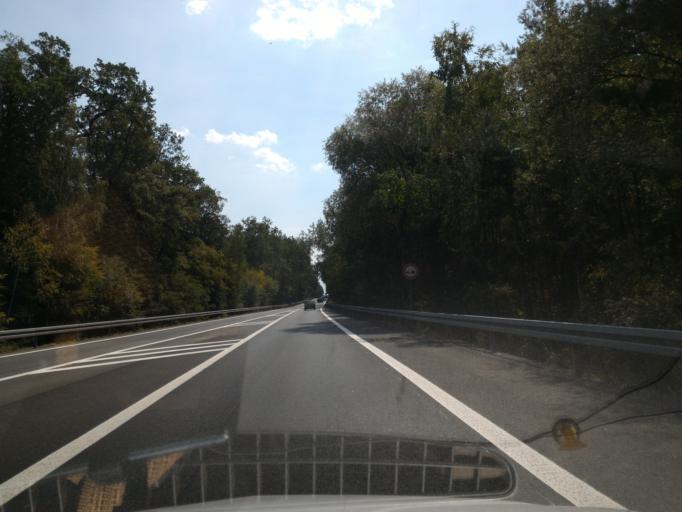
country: CZ
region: Central Bohemia
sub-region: Okres Nymburk
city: Podebrady
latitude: 50.1140
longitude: 15.1288
